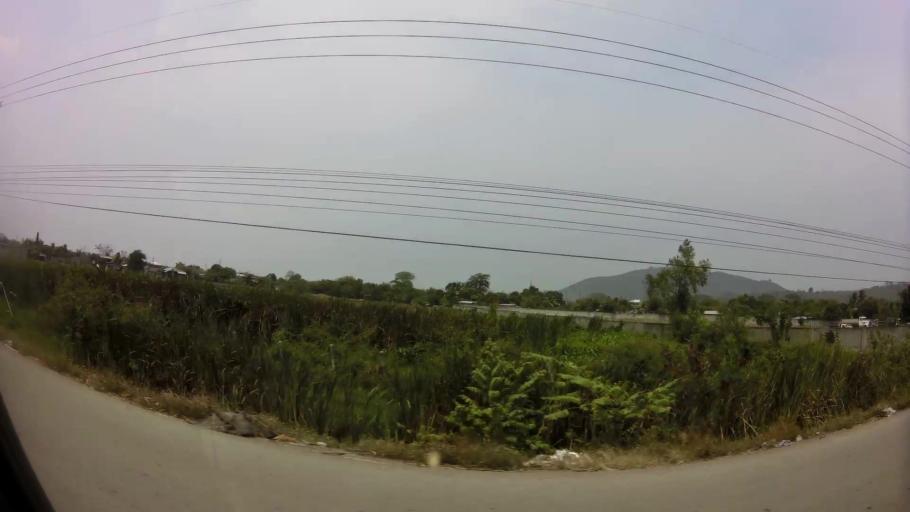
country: HN
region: Cortes
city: El Plan
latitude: 15.2990
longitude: -87.9817
